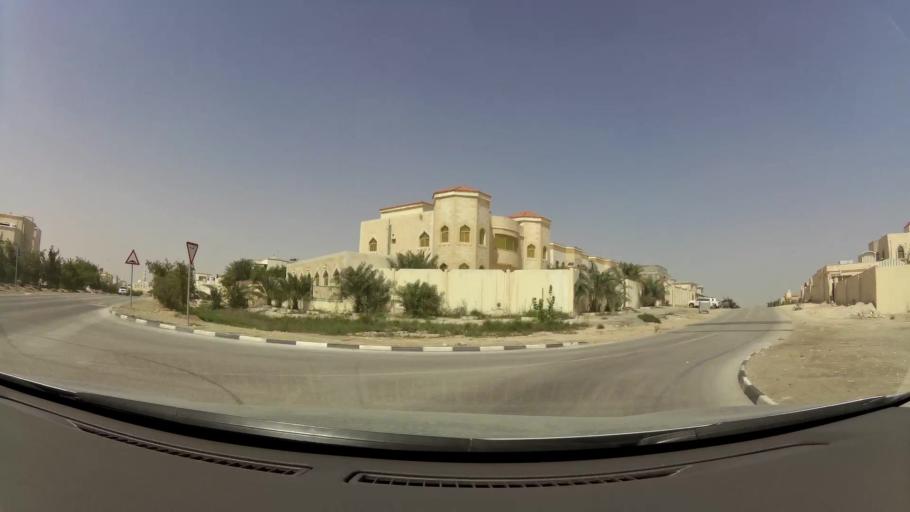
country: QA
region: Baladiyat Umm Salal
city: Umm Salal Muhammad
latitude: 25.3855
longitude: 51.4180
